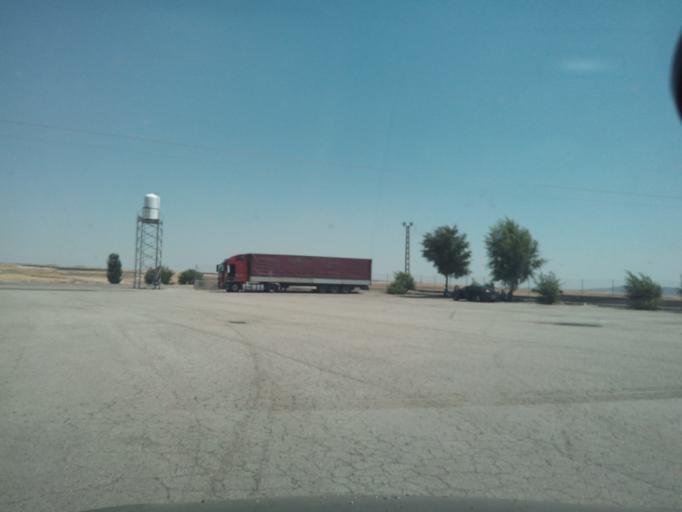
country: ES
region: Castille-La Mancha
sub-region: Province of Toledo
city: Tembleque
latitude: 39.7659
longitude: -3.4796
